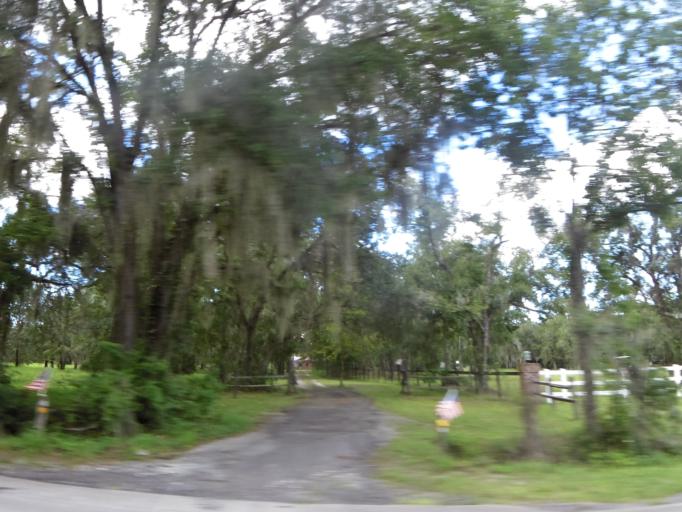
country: US
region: Florida
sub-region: Saint Johns County
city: Saint Augustine South
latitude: 29.8400
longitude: -81.5002
